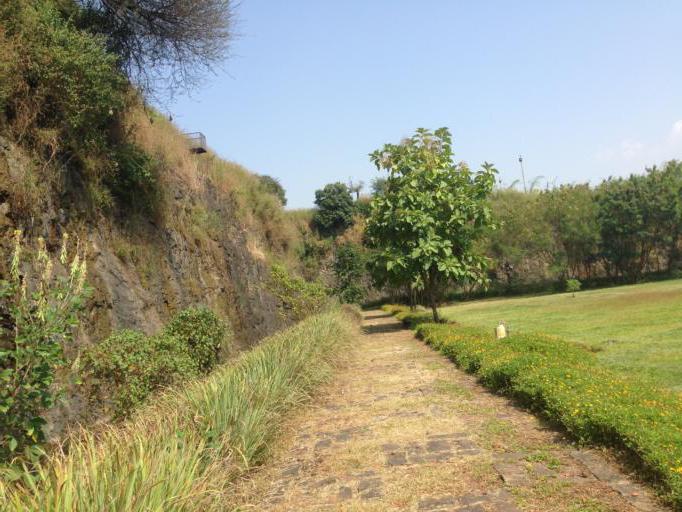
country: IN
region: Karnataka
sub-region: Belgaum
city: Belgaum
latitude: 15.8228
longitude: 74.4799
